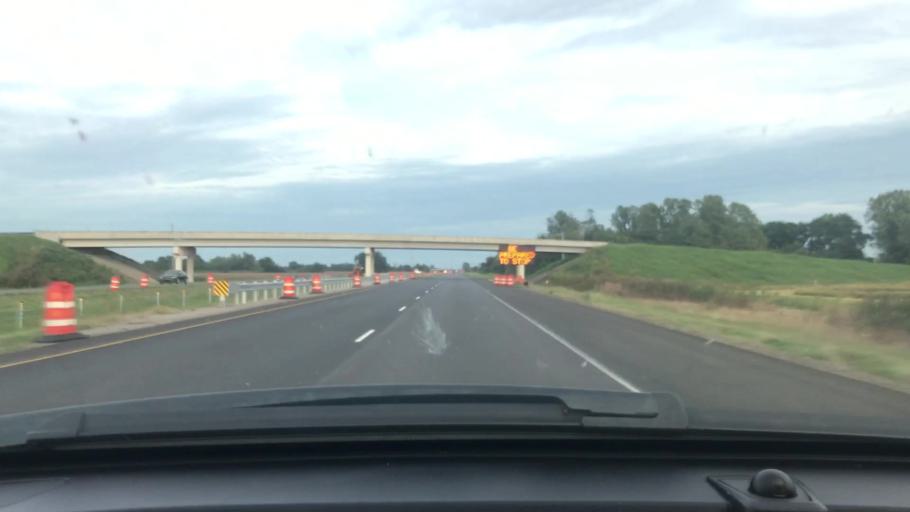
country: US
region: Arkansas
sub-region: Poinsett County
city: Trumann
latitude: 35.6552
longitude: -90.5376
